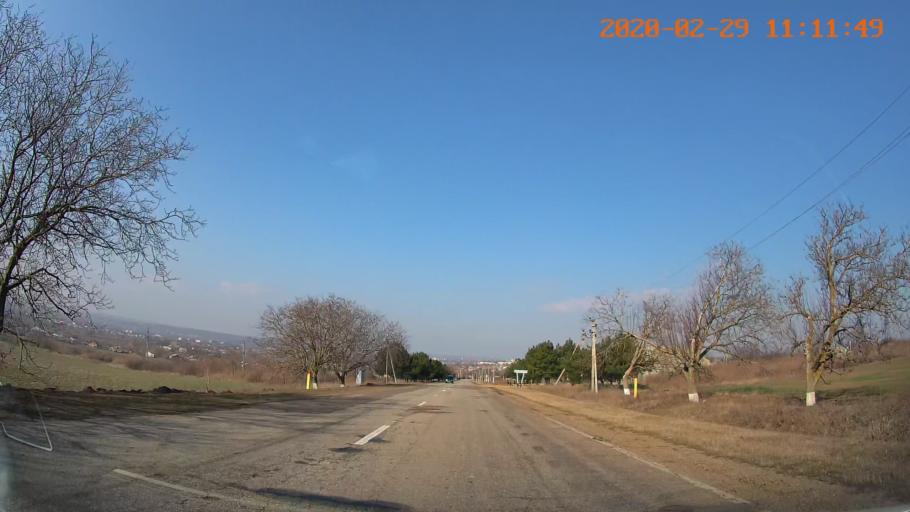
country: MD
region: Telenesti
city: Dubasari
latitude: 47.2582
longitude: 29.1924
